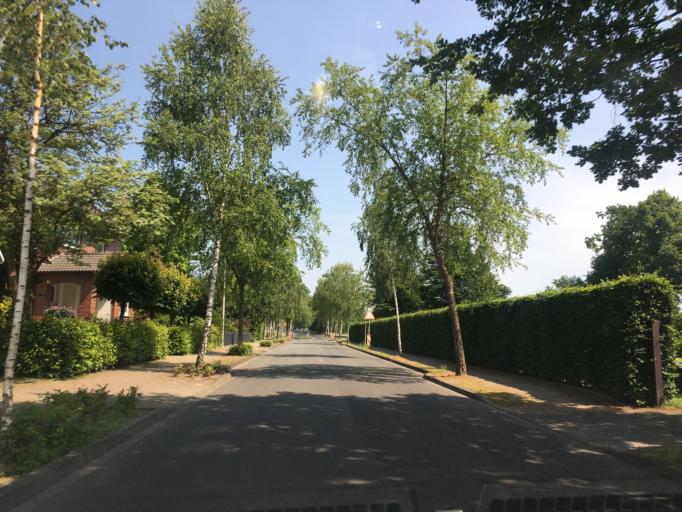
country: DE
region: North Rhine-Westphalia
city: Olfen
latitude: 51.7146
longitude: 7.3831
